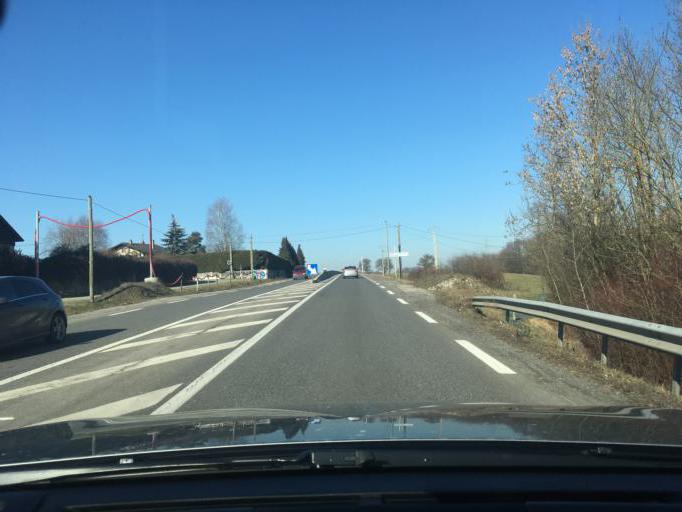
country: FR
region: Rhone-Alpes
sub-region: Departement de la Haute-Savoie
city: Cranves-Sales
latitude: 46.1975
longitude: 6.2917
